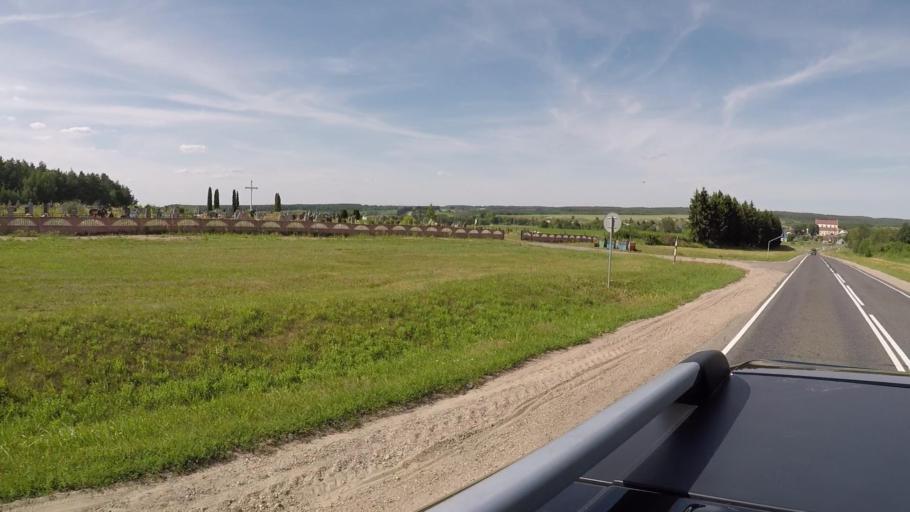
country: BY
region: Grodnenskaya
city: Hal'shany
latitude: 54.2494
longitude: 26.0038
